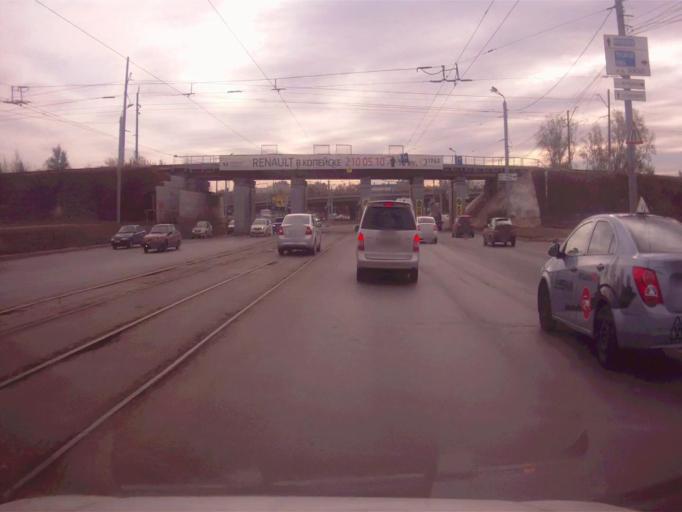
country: RU
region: Chelyabinsk
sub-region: Gorod Chelyabinsk
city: Chelyabinsk
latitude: 55.1528
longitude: 61.4427
